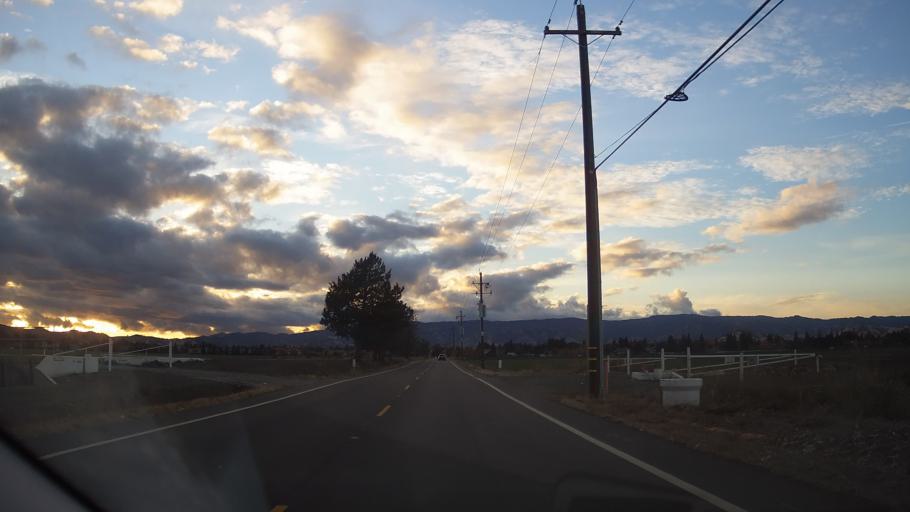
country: US
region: California
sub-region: Solano County
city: Hartley
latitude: 38.3588
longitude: -121.9243
